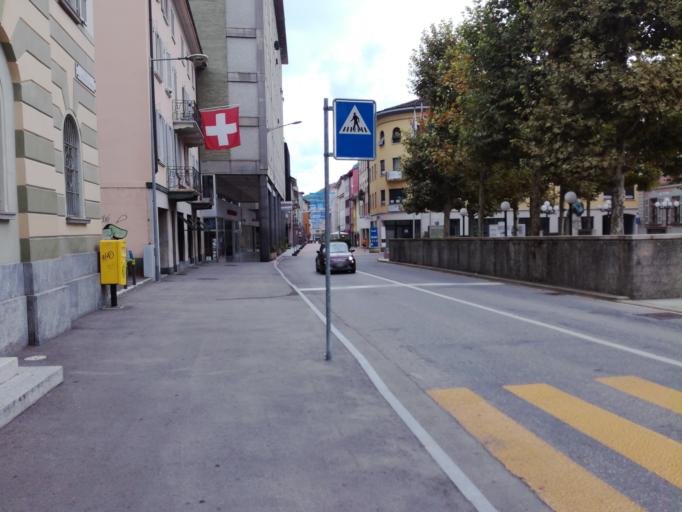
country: CH
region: Ticino
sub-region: Mendrisio District
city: Chiasso
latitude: 45.8354
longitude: 9.0275
